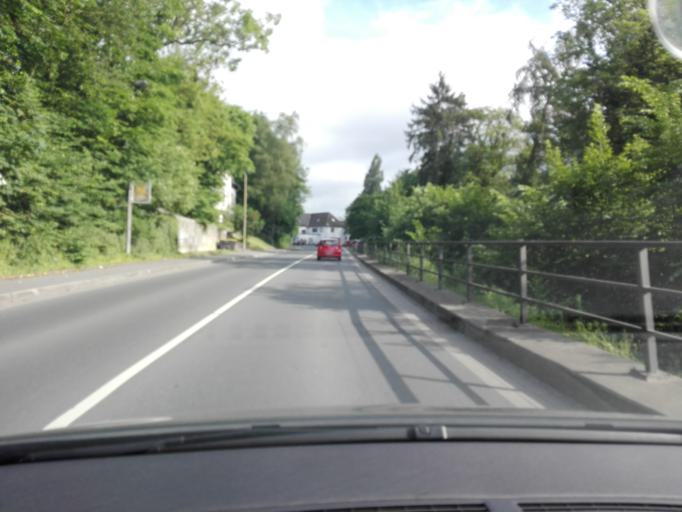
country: DE
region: North Rhine-Westphalia
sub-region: Regierungsbezirk Arnsberg
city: Menden
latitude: 51.4448
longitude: 7.7785
